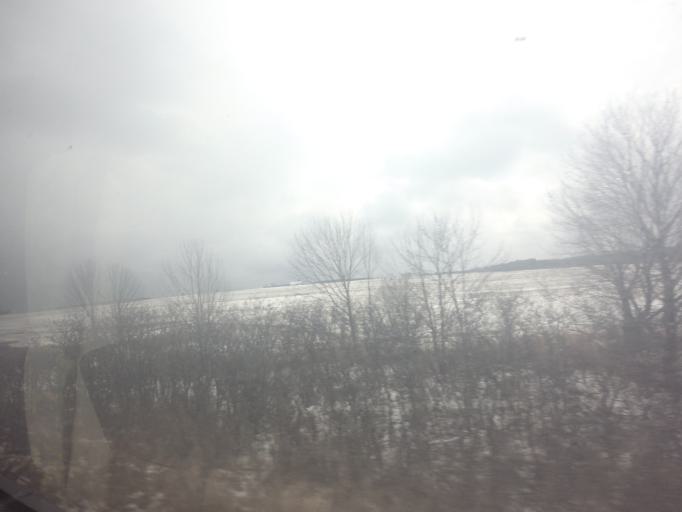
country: CA
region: Ontario
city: Cobourg
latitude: 43.9475
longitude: -78.3684
